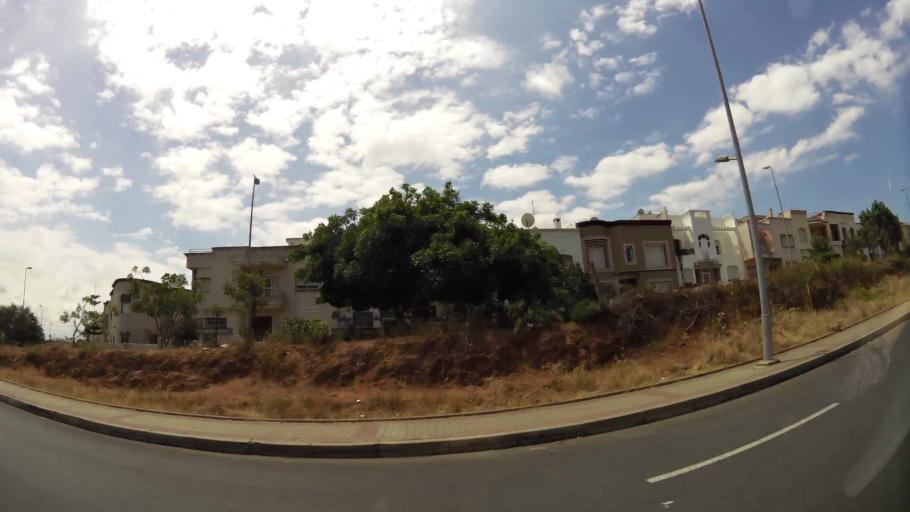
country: MA
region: Gharb-Chrarda-Beni Hssen
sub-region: Kenitra Province
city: Kenitra
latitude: 34.2773
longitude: -6.6071
